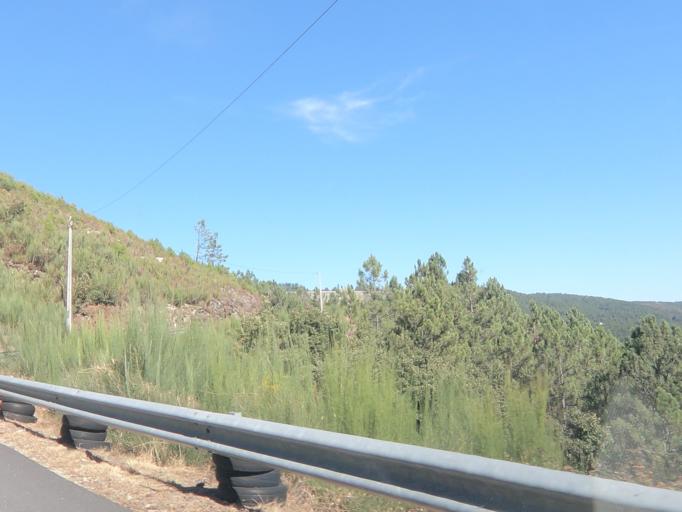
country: PT
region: Vila Real
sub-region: Santa Marta de Penaguiao
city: Santa Marta de Penaguiao
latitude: 41.2707
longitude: -7.8729
